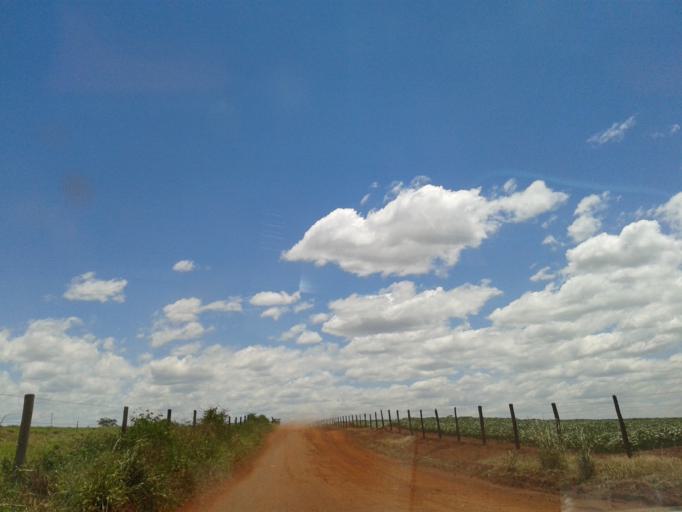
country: BR
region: Minas Gerais
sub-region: Centralina
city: Centralina
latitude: -18.7127
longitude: -49.2145
